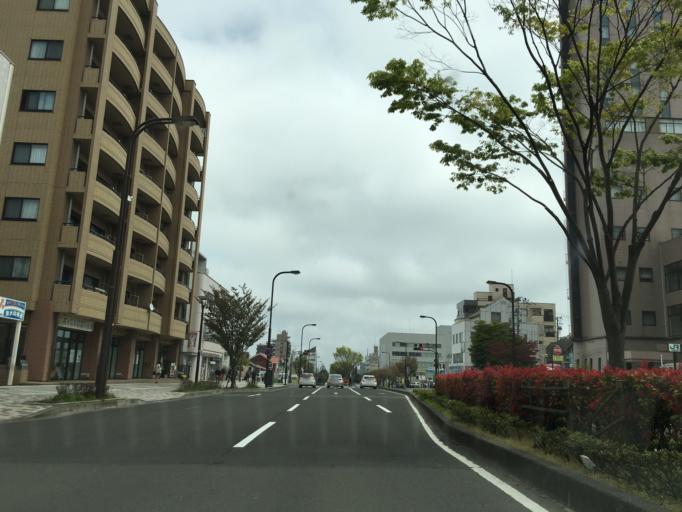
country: JP
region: Miyagi
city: Sendai-shi
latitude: 38.2589
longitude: 140.8938
